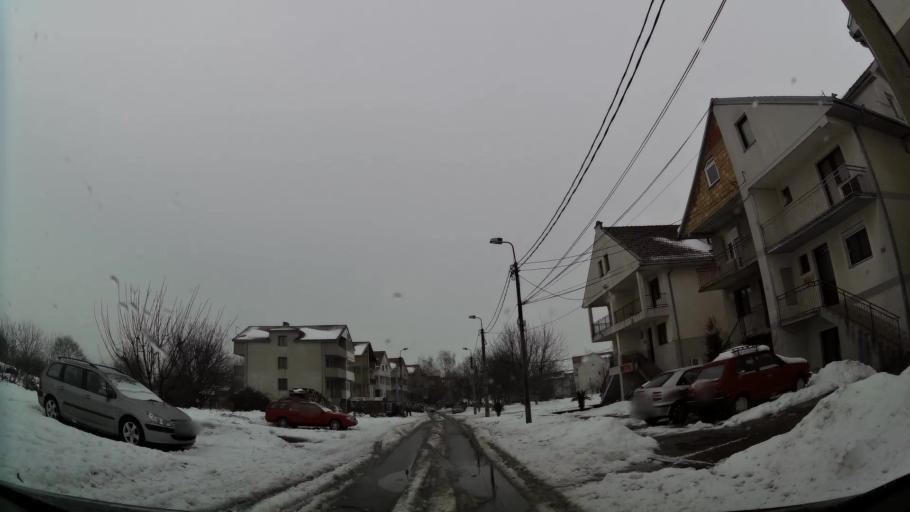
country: RS
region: Central Serbia
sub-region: Belgrade
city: Zemun
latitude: 44.8730
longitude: 20.3309
